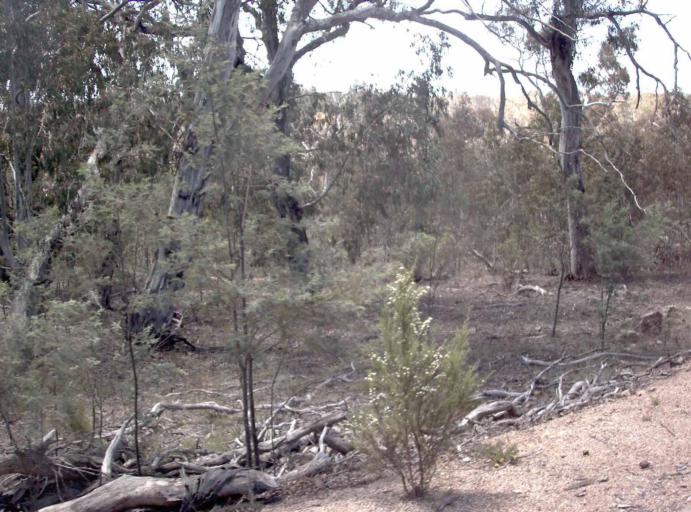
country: AU
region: New South Wales
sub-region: Snowy River
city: Jindabyne
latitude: -37.0701
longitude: 148.2835
